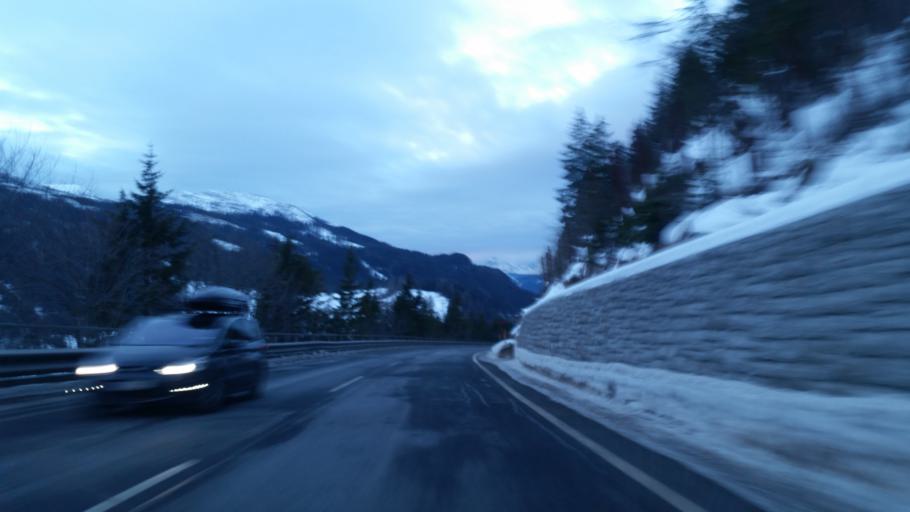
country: AT
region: Salzburg
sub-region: Politischer Bezirk Sankt Johann im Pongau
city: Untertauern
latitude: 47.2583
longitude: 13.4991
